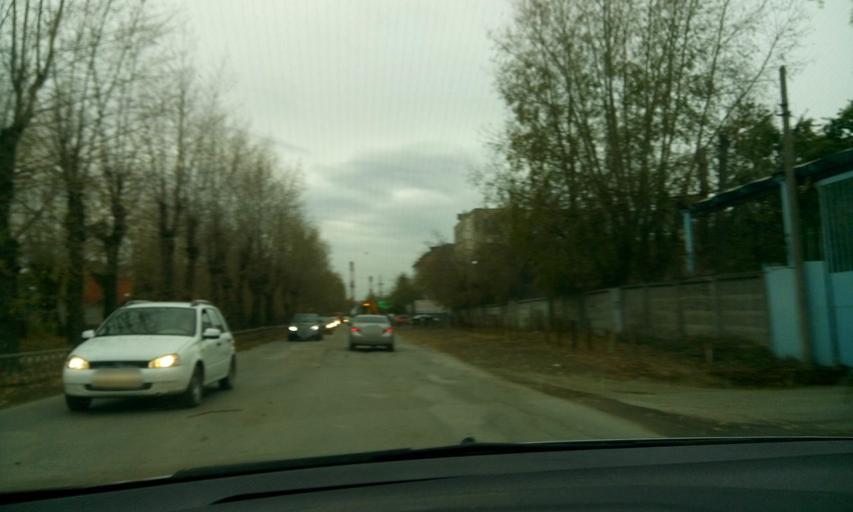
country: RU
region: Sverdlovsk
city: Yekaterinburg
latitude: 56.8759
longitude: 60.6179
